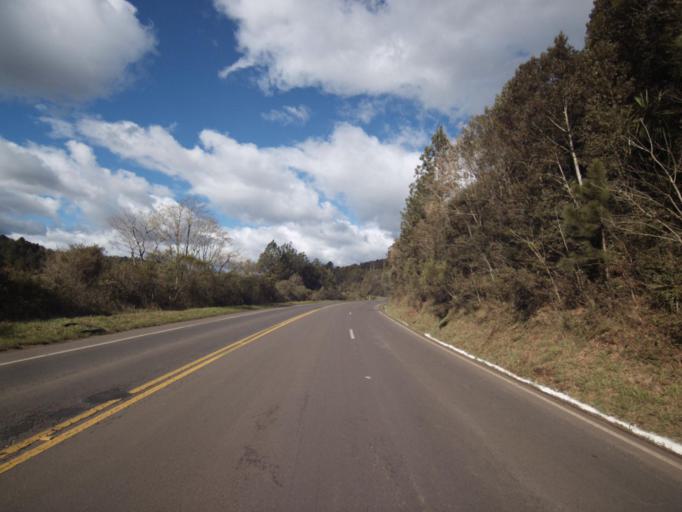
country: BR
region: Santa Catarina
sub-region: Joacaba
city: Joacaba
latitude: -27.0564
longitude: -51.6866
